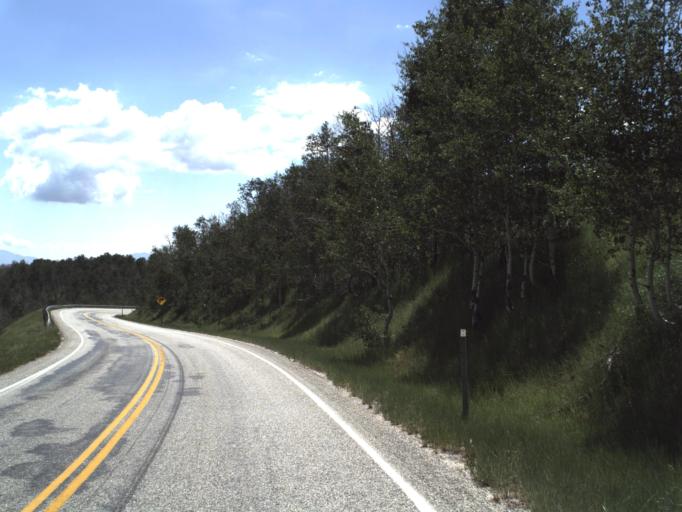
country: US
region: Utah
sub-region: Weber County
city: Wolf Creek
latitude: 41.4048
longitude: -111.5403
